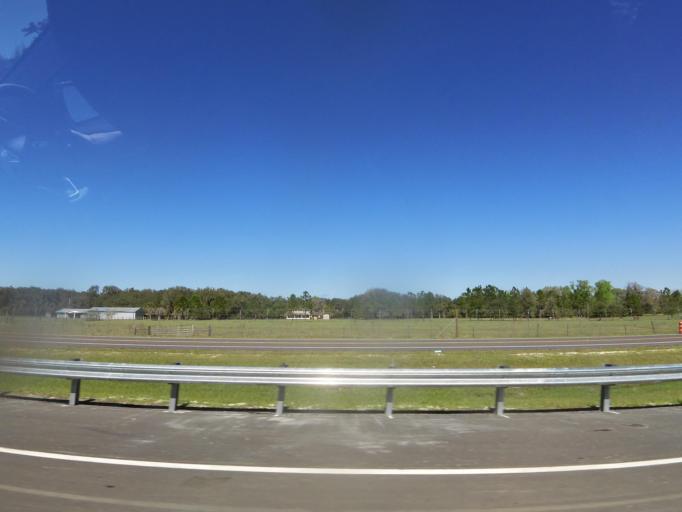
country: US
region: Florida
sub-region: Lake County
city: Mount Plymouth
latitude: 28.8149
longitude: -81.4866
